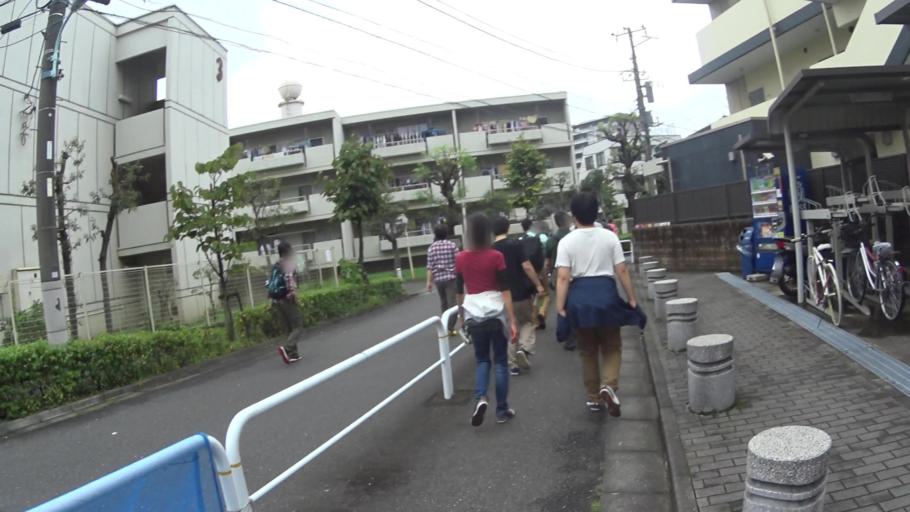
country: JP
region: Tokyo
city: Tokyo
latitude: 35.7399
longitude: 139.6800
